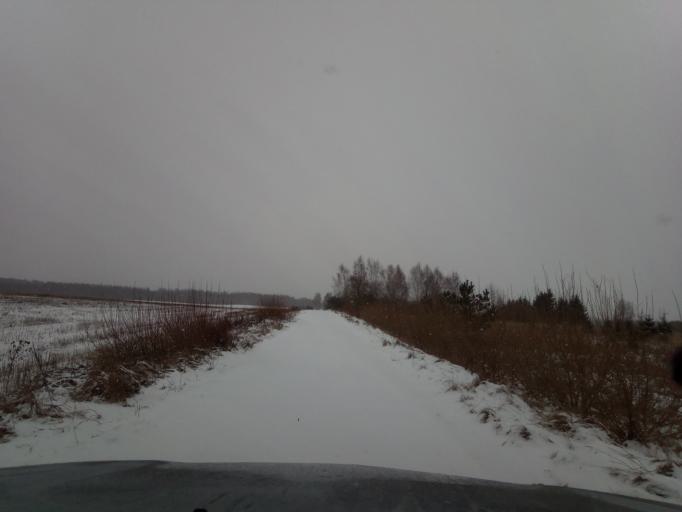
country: LT
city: Ramygala
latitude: 55.5879
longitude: 24.3642
